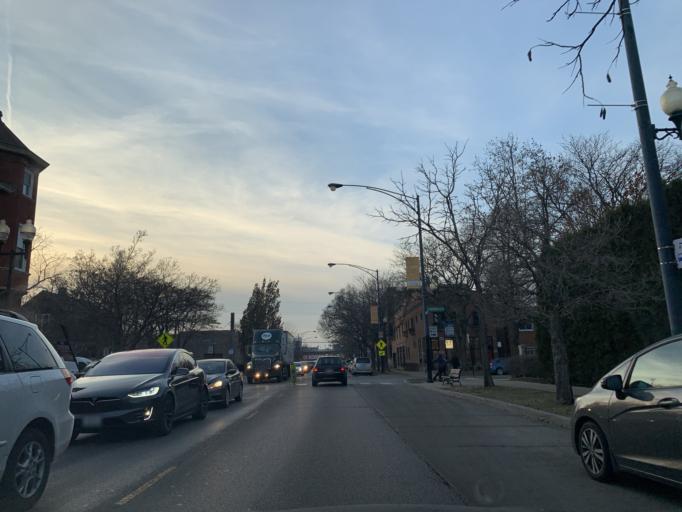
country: US
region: Illinois
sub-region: Cook County
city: Lincolnwood
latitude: 41.9616
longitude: -87.6719
